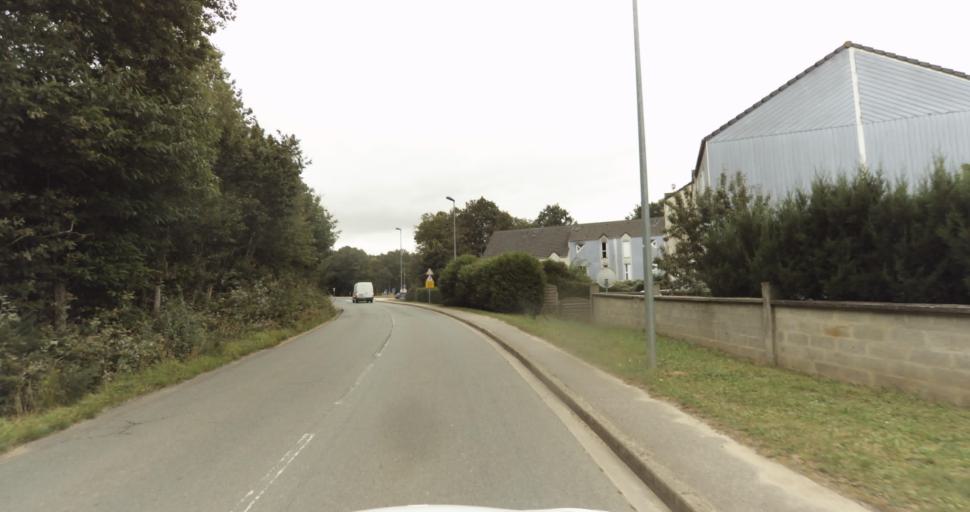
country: FR
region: Haute-Normandie
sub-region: Departement de l'Eure
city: Gravigny
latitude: 49.0352
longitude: 1.1752
